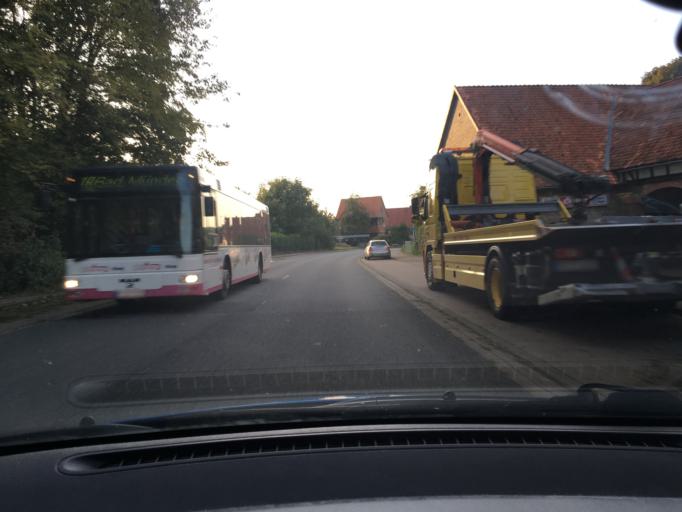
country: DE
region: Lower Saxony
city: Messenkamp
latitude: 52.2338
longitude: 9.4156
